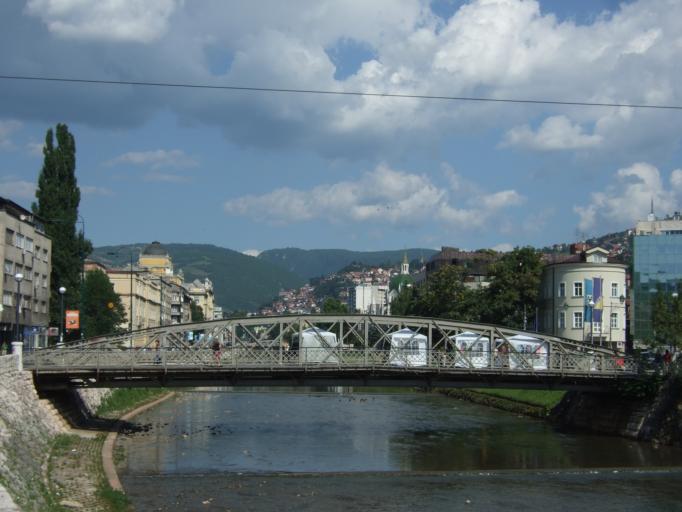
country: BA
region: Federation of Bosnia and Herzegovina
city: Kobilja Glava
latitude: 43.8562
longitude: 18.4133
